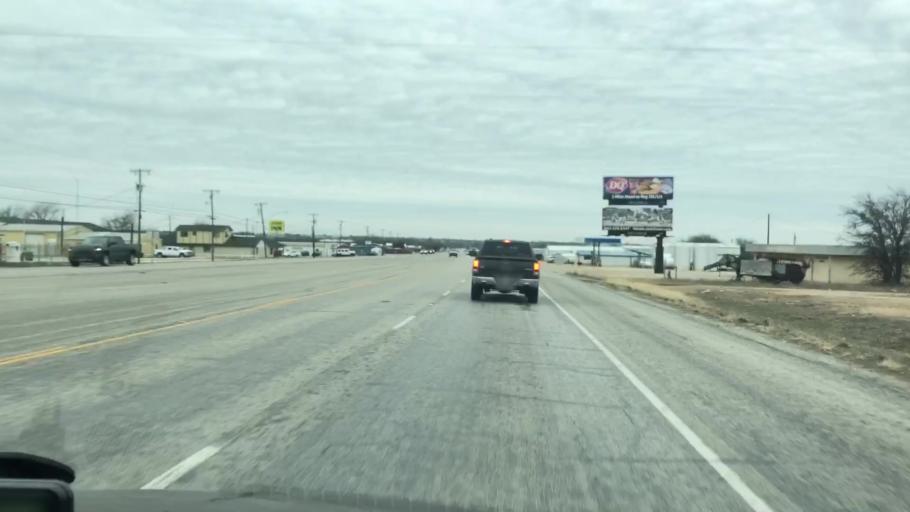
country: US
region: Texas
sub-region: Jack County
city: Jacksboro
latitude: 33.1994
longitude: -98.1482
